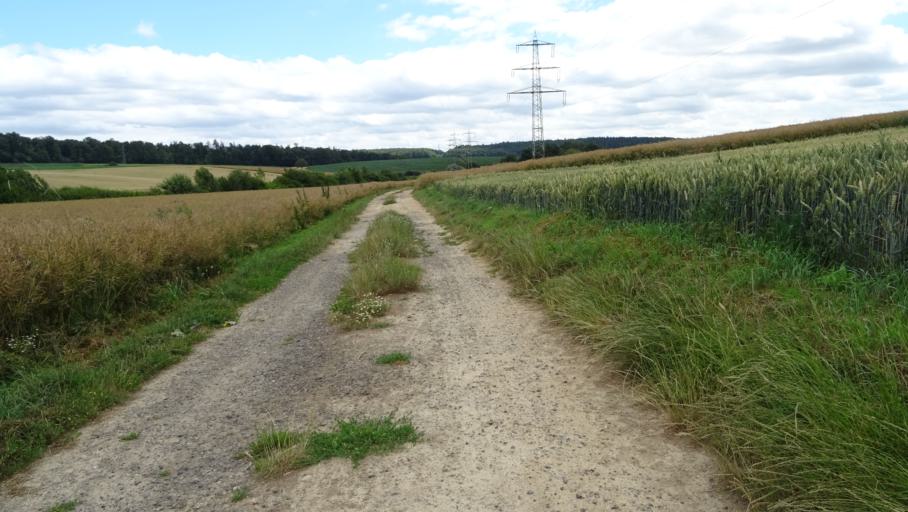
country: DE
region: Baden-Wuerttemberg
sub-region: Karlsruhe Region
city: Neunkirchen
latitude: 49.3799
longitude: 9.0248
